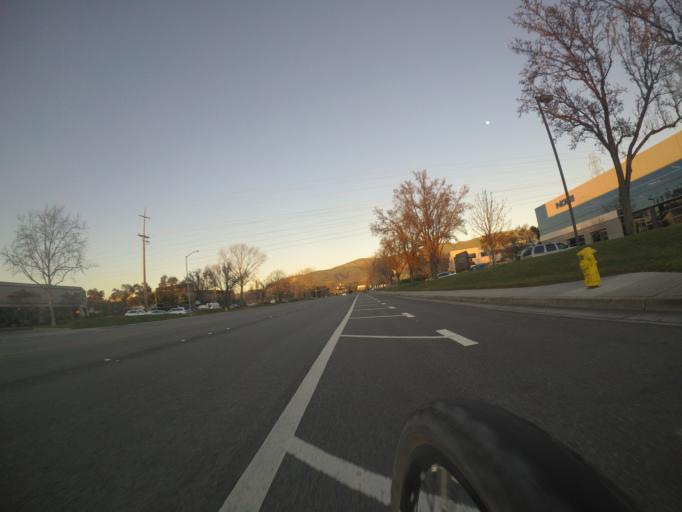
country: US
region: California
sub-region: Santa Clara County
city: Milpitas
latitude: 37.4751
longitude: -121.9391
